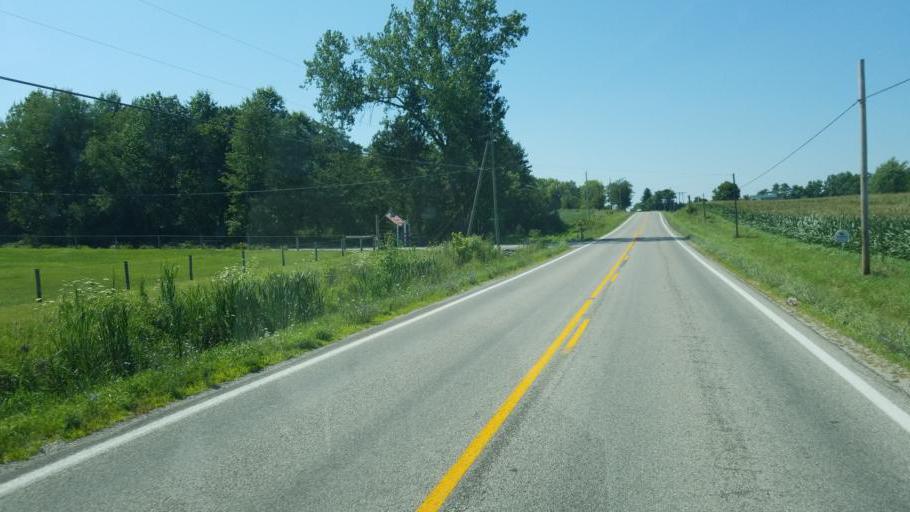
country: US
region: Ohio
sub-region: Morrow County
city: Cardington
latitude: 40.4434
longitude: -82.8237
